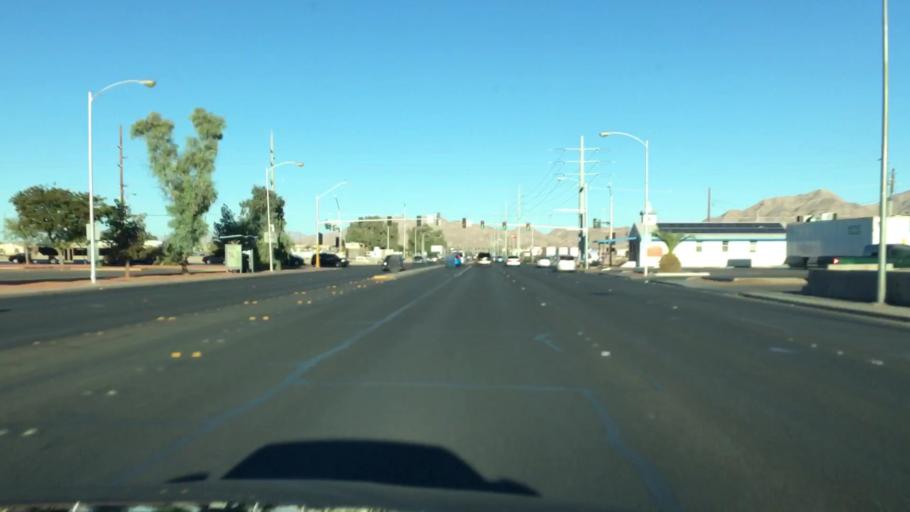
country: US
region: Nevada
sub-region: Clark County
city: North Las Vegas
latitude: 36.2176
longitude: -115.0999
